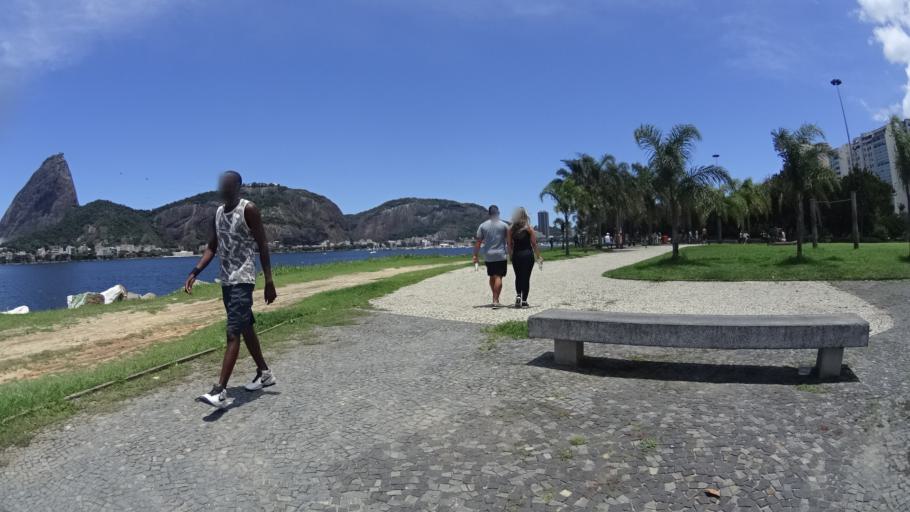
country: BR
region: Rio de Janeiro
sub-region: Rio De Janeiro
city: Rio de Janeiro
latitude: -22.9386
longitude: -43.1689
